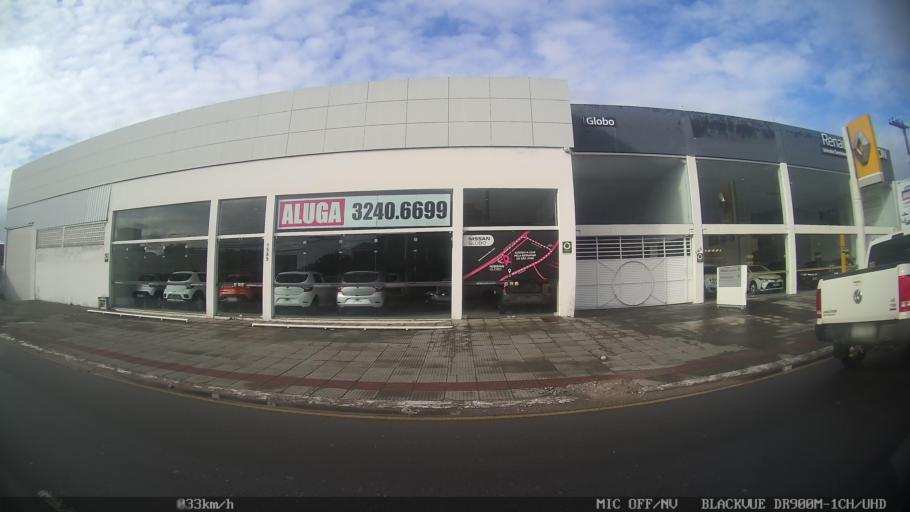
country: BR
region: Santa Catarina
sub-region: Sao Jose
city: Campinas
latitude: -27.6044
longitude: -48.6227
